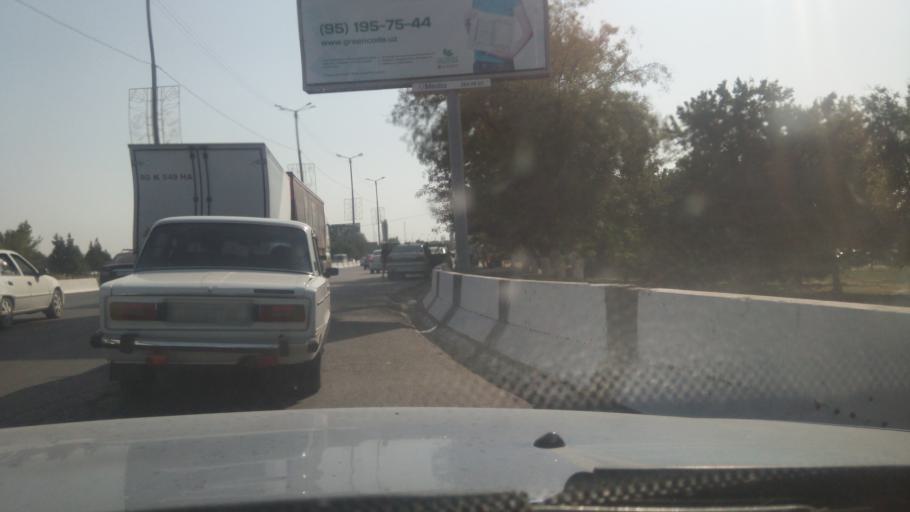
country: UZ
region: Toshkent Shahri
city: Tashkent
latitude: 41.2401
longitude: 69.1690
